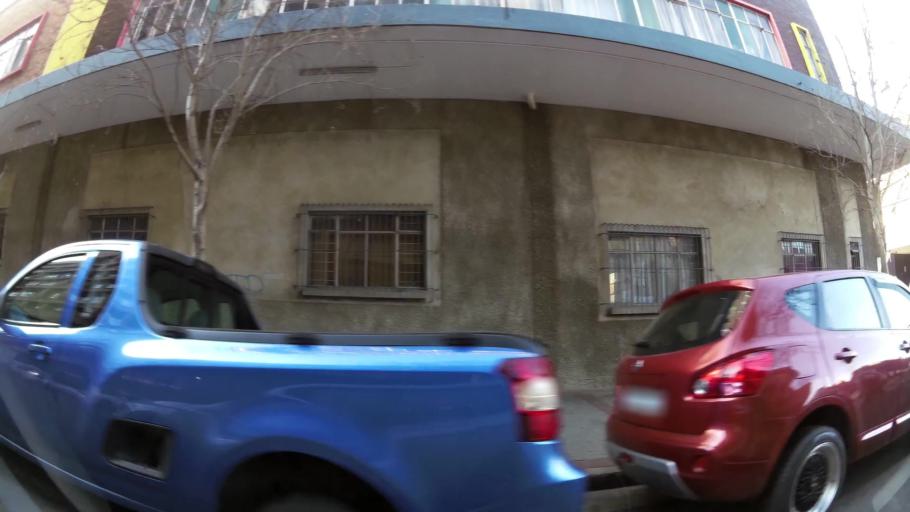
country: ZA
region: Gauteng
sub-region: City of Johannesburg Metropolitan Municipality
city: Johannesburg
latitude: -26.2046
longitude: 28.0601
